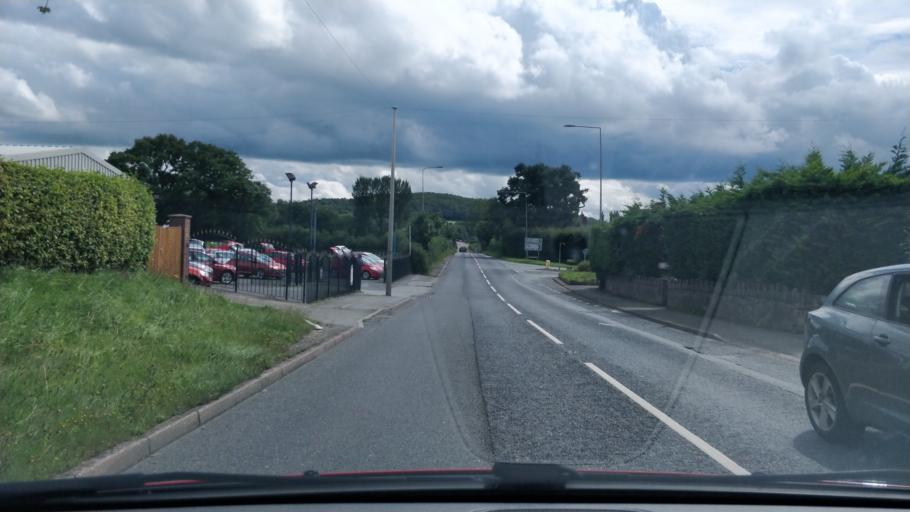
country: GB
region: Wales
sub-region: County of Flintshire
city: Hope
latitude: 53.1204
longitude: -3.0324
